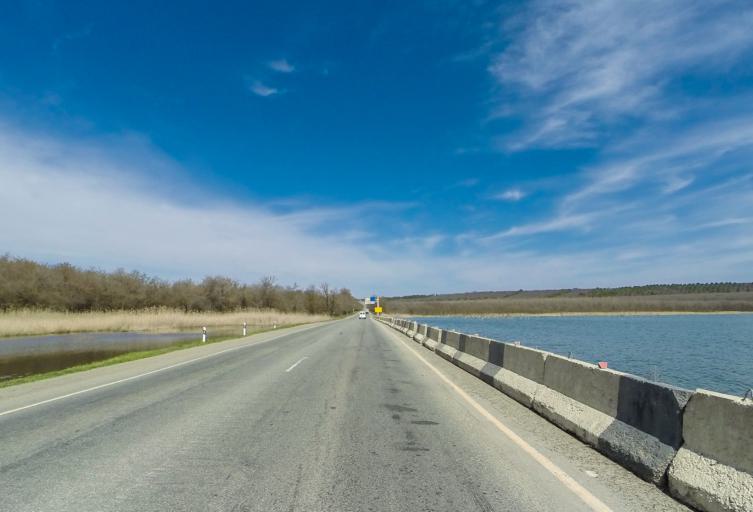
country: RU
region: Stavropol'skiy
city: Goryachevodskiy
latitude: 43.9610
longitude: 43.1470
